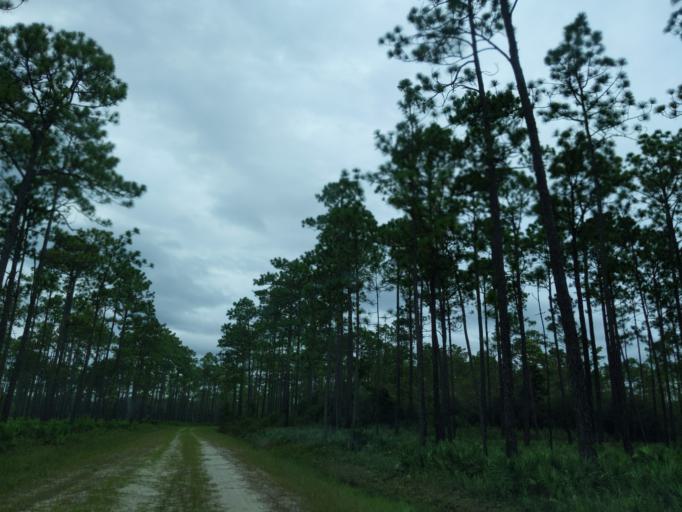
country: US
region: Florida
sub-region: Gadsden County
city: Midway
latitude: 30.3770
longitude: -84.4760
